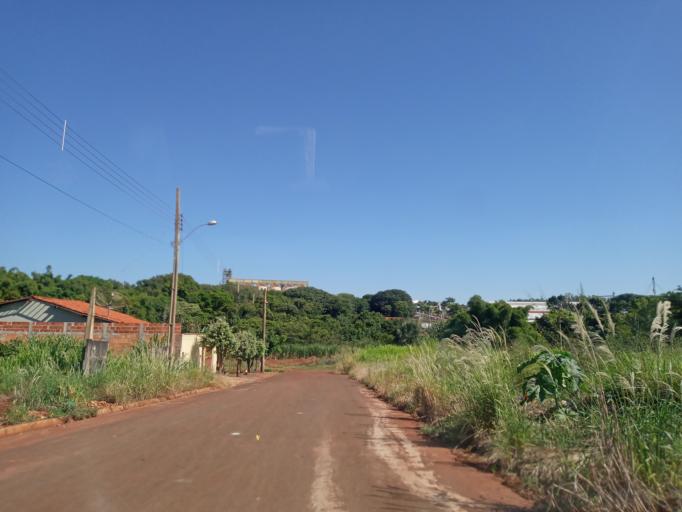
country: BR
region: Minas Gerais
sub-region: Ituiutaba
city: Ituiutaba
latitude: -18.9708
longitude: -49.4880
